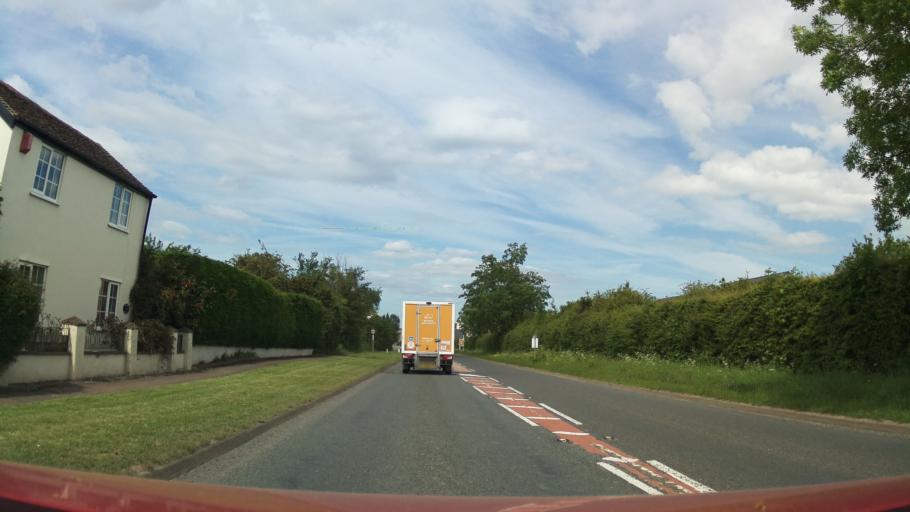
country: GB
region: England
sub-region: Worcestershire
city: Leigh
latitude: 52.1515
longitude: -2.3305
